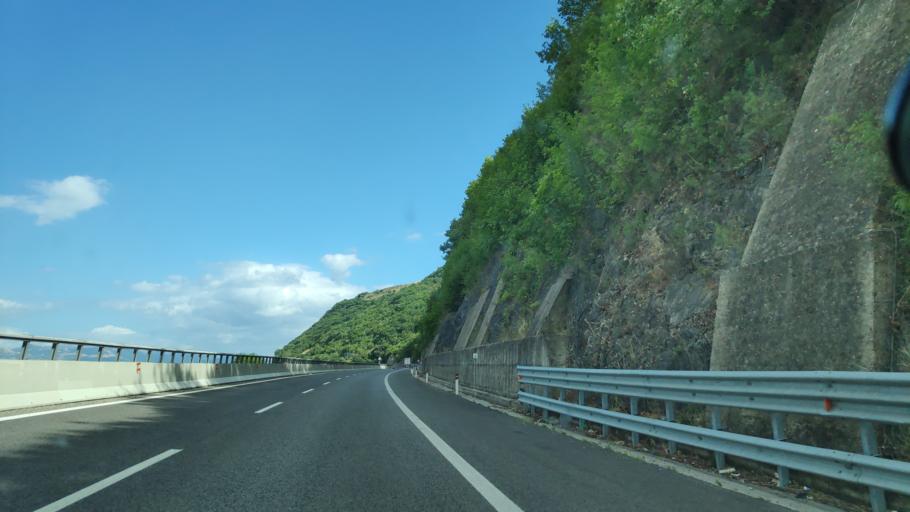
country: IT
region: Campania
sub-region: Provincia di Salerno
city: Sicignano degli Alburni
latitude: 40.5957
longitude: 15.3213
